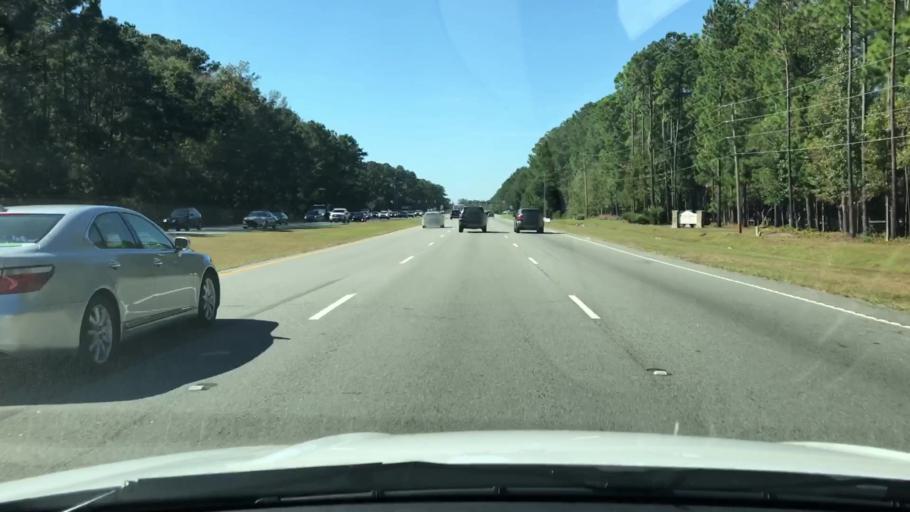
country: US
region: South Carolina
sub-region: Beaufort County
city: Bluffton
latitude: 32.2907
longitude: -80.9045
